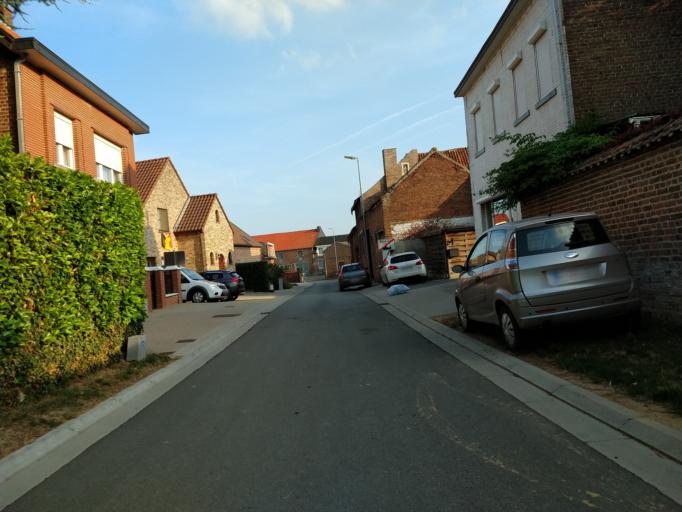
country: BE
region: Flanders
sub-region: Provincie Vlaams-Brabant
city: Boutersem
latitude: 50.8110
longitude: 4.8401
